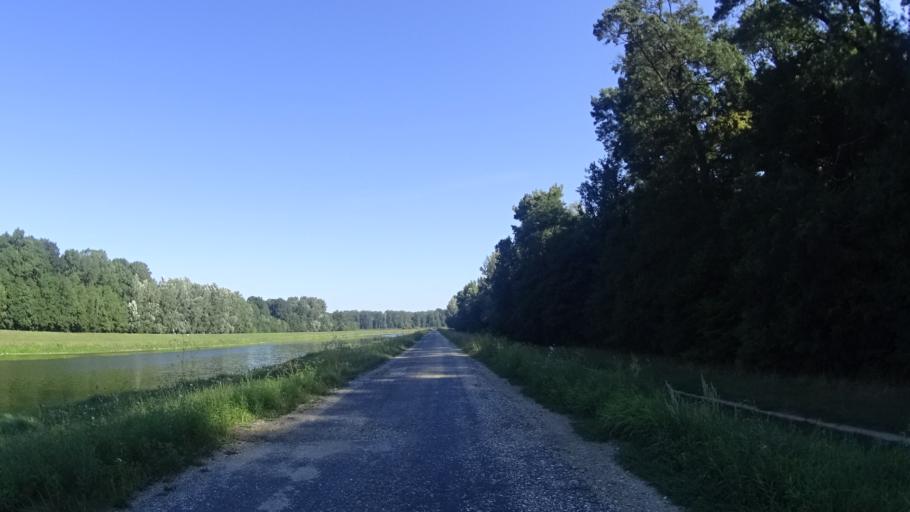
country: CZ
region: South Moravian
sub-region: Okres Breclav
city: Lanzhot
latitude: 48.7000
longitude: 16.9989
